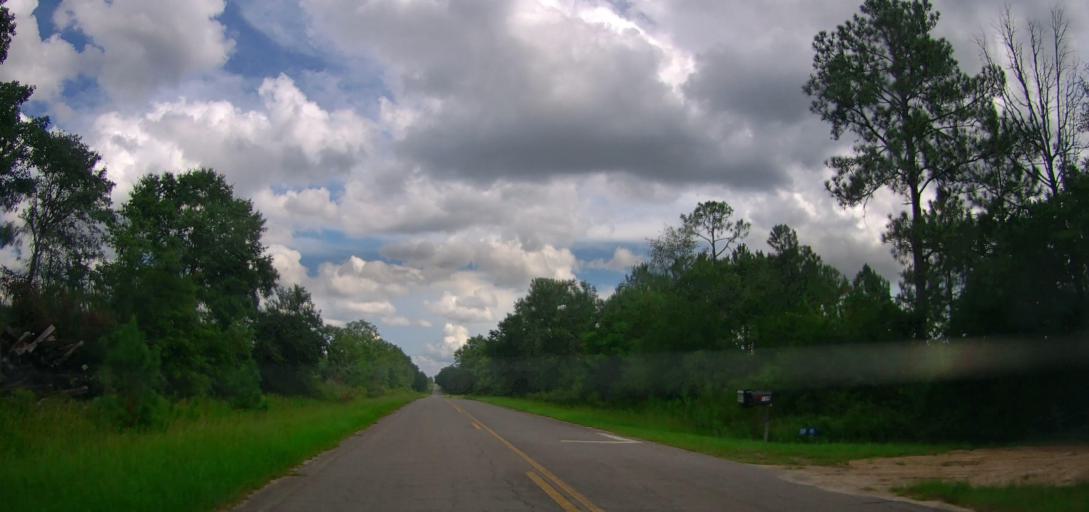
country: US
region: Georgia
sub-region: Taylor County
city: Butler
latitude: 32.5927
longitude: -84.3692
